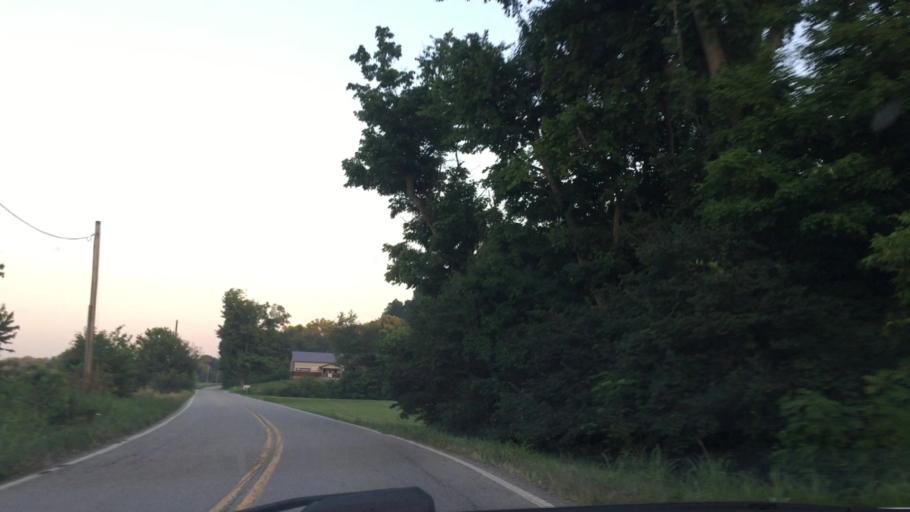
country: US
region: Kentucky
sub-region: Carroll County
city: Carrollton
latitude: 38.6741
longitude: -85.1961
